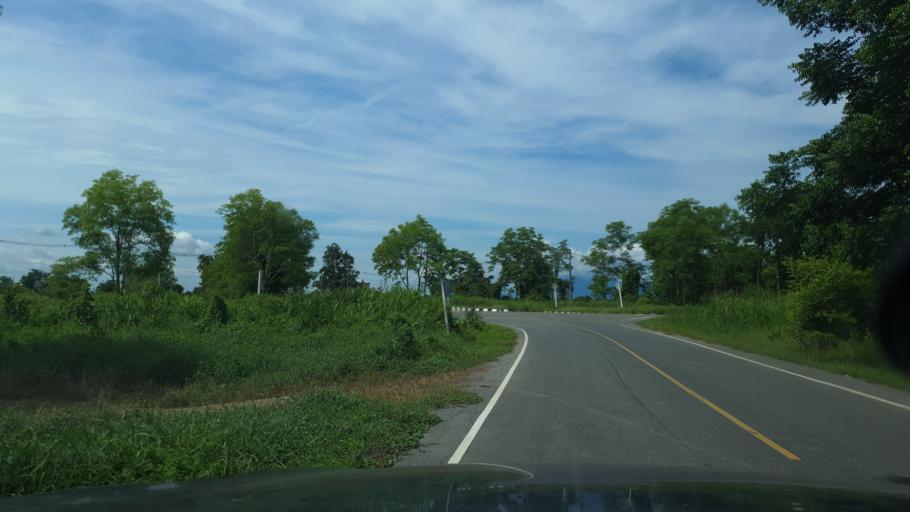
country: TH
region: Sukhothai
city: Si Samrong
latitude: 17.1126
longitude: 99.7774
